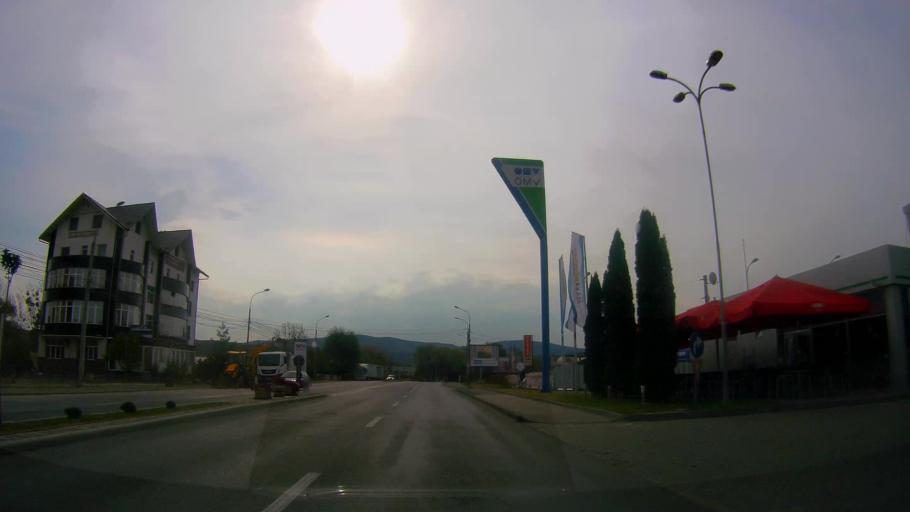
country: RO
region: Salaj
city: Zalau
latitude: 47.1983
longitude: 23.0585
